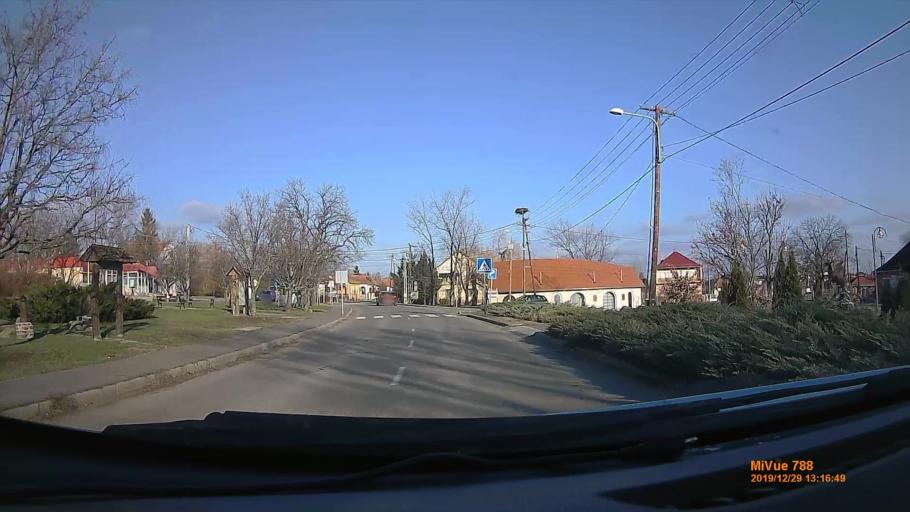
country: HU
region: Heves
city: Domoszlo
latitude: 47.8274
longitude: 20.1185
